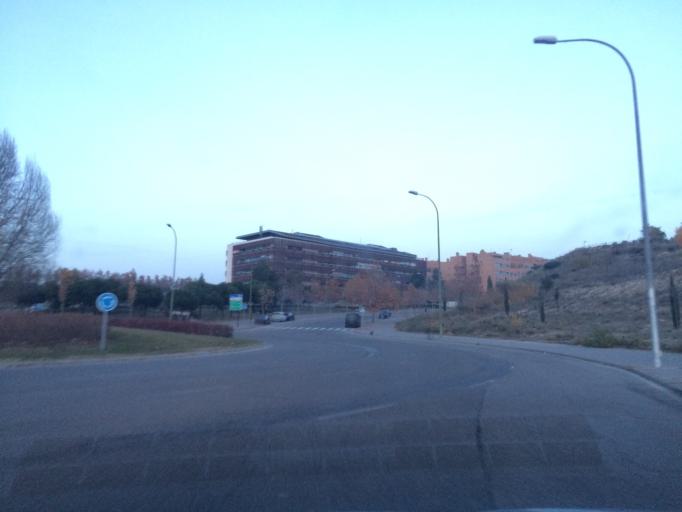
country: ES
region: Madrid
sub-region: Provincia de Madrid
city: Fuencarral-El Pardo
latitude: 40.5027
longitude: -3.7133
